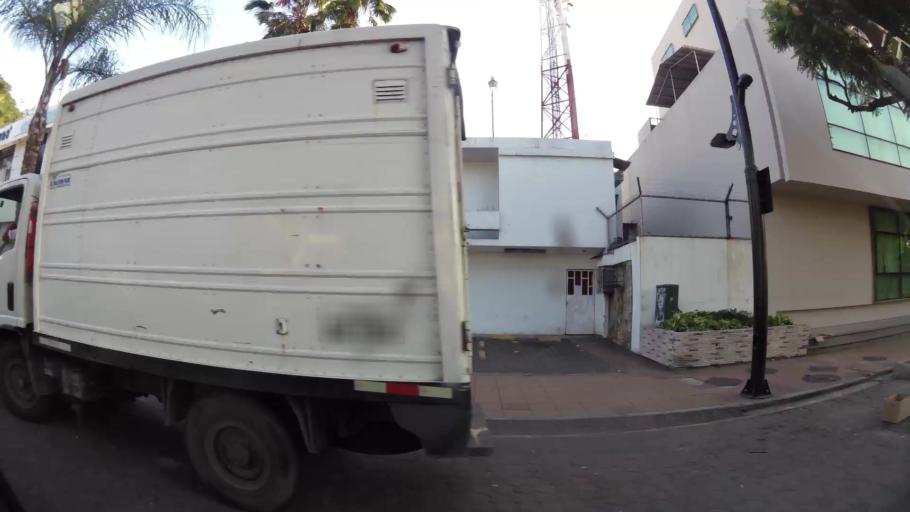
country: EC
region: Guayas
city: Guayaquil
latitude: -2.1755
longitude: -79.9051
